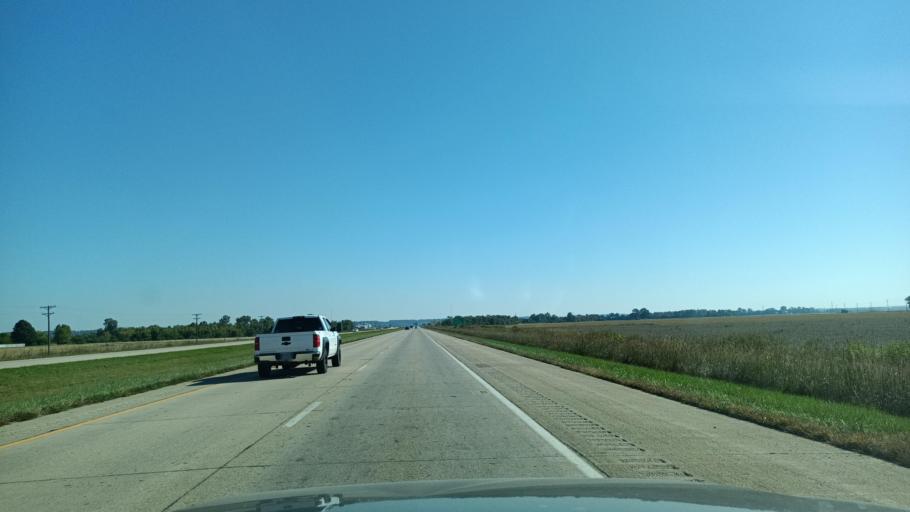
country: US
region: Missouri
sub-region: Marion County
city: Hannibal
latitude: 39.7311
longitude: -91.3258
